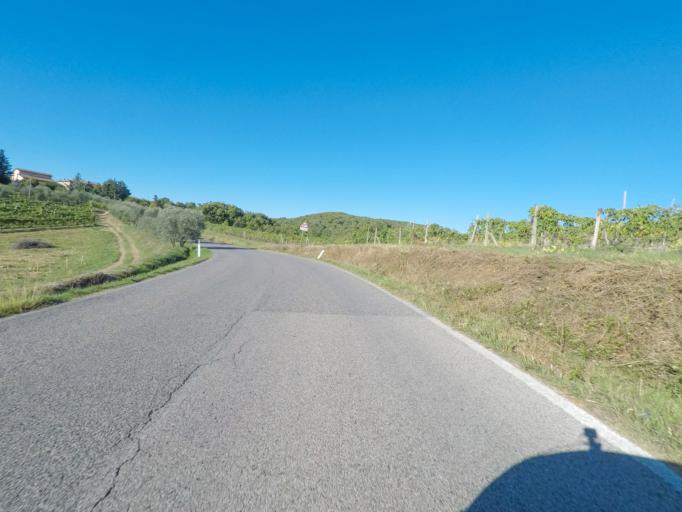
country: IT
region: Tuscany
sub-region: Provincia di Siena
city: Belverde
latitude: 43.4014
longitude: 11.3526
